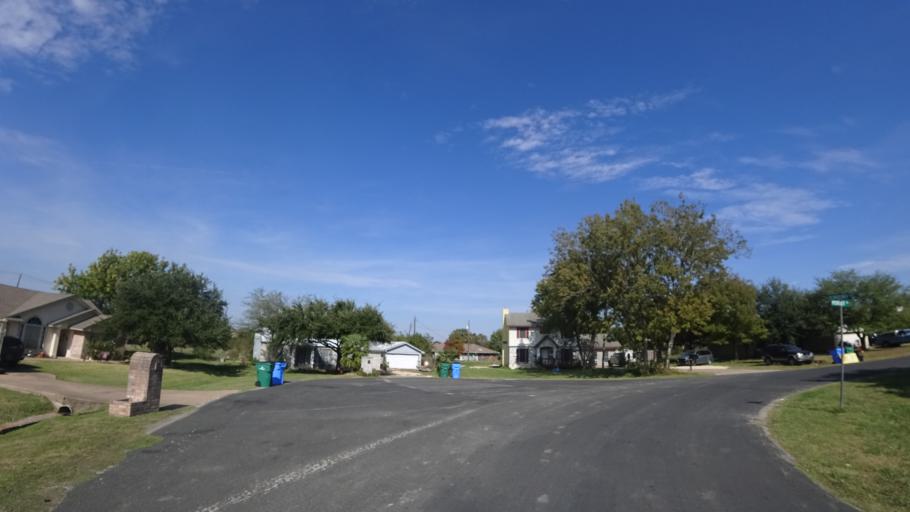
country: US
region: Texas
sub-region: Travis County
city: Pflugerville
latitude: 30.4155
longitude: -97.6309
